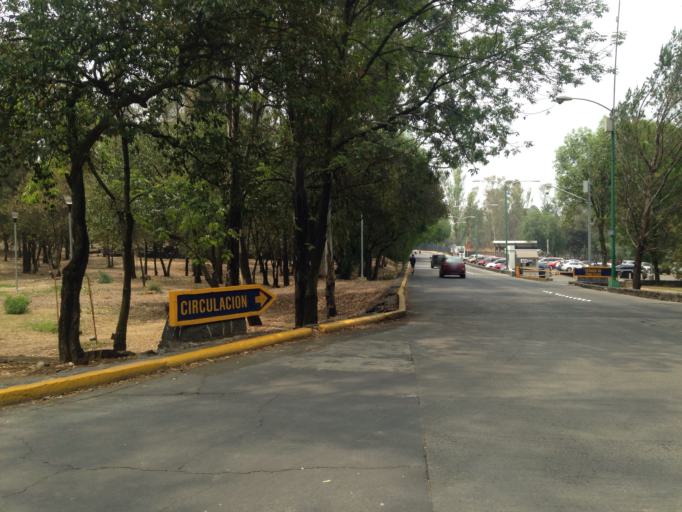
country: MX
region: Mexico City
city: Magdalena Contreras
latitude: 19.3242
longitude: -99.1878
